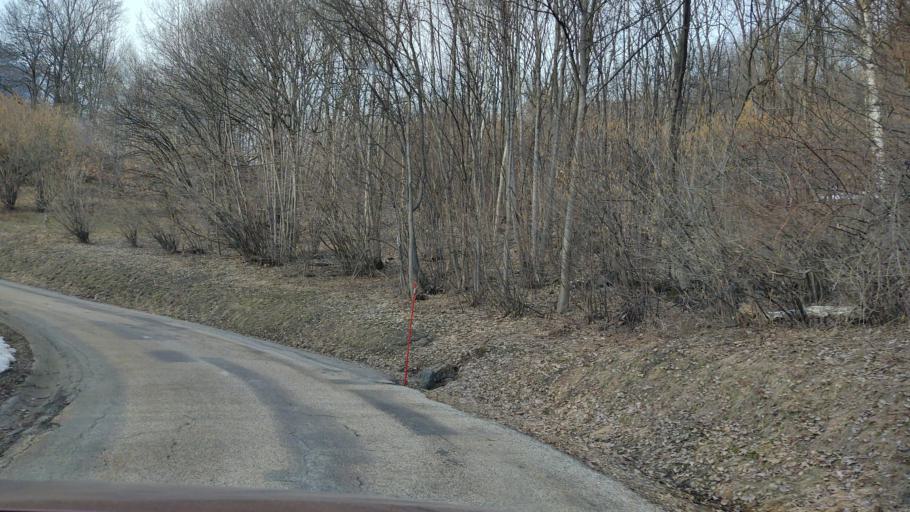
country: FR
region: Rhone-Alpes
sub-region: Departement de la Savoie
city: Saint-Michel-de-Maurienne
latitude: 45.2406
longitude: 6.4698
